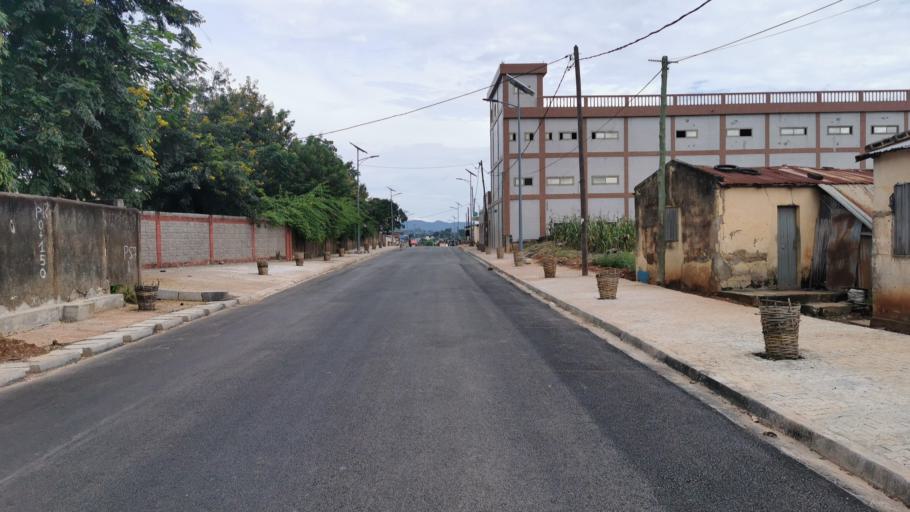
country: TG
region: Kara
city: Kara
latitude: 9.5549
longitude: 1.1919
